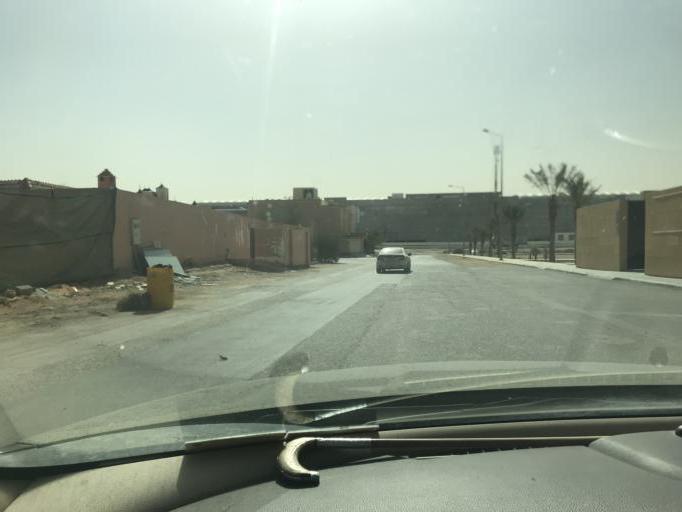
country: SA
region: Ar Riyad
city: Riyadh
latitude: 24.8279
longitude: 46.7314
